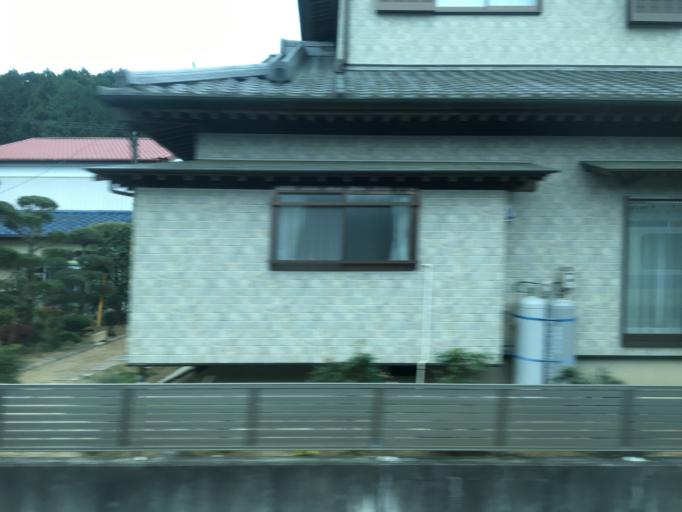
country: JP
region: Ibaraki
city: Iwase
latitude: 36.3585
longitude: 140.1158
